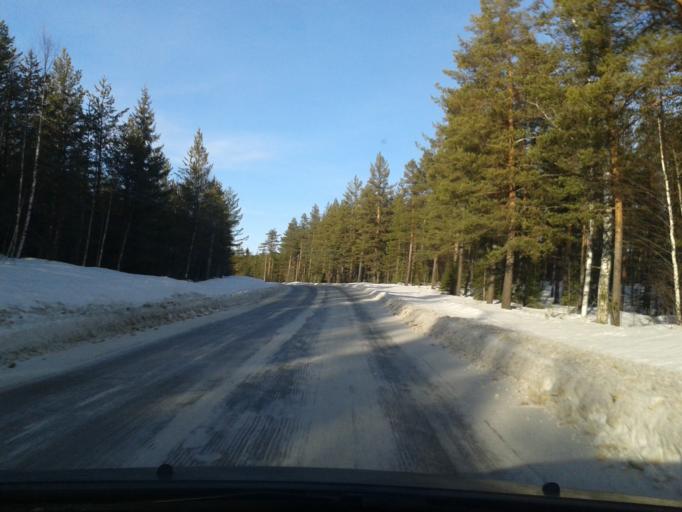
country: SE
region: Vaesternorrland
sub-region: OErnskoeldsviks Kommun
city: Bredbyn
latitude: 63.7380
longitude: 17.7449
